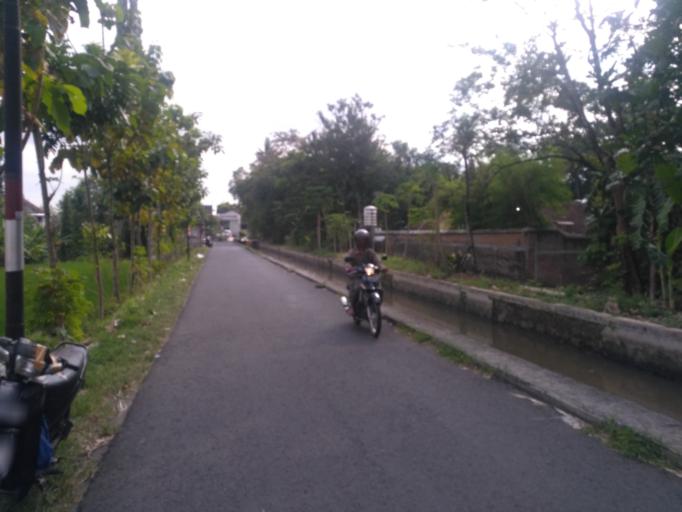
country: ID
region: Daerah Istimewa Yogyakarta
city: Yogyakarta
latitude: -7.7600
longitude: 110.3685
